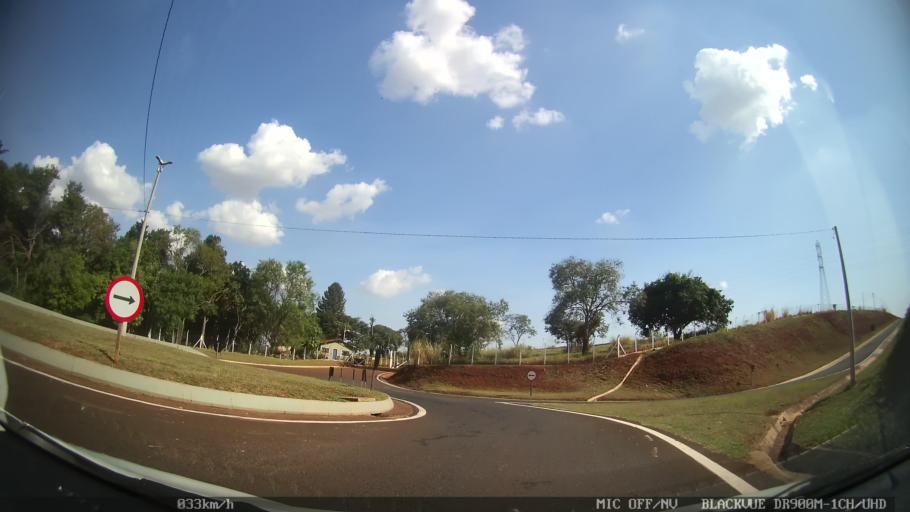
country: BR
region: Sao Paulo
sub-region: Ribeirao Preto
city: Ribeirao Preto
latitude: -21.2049
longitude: -47.8615
